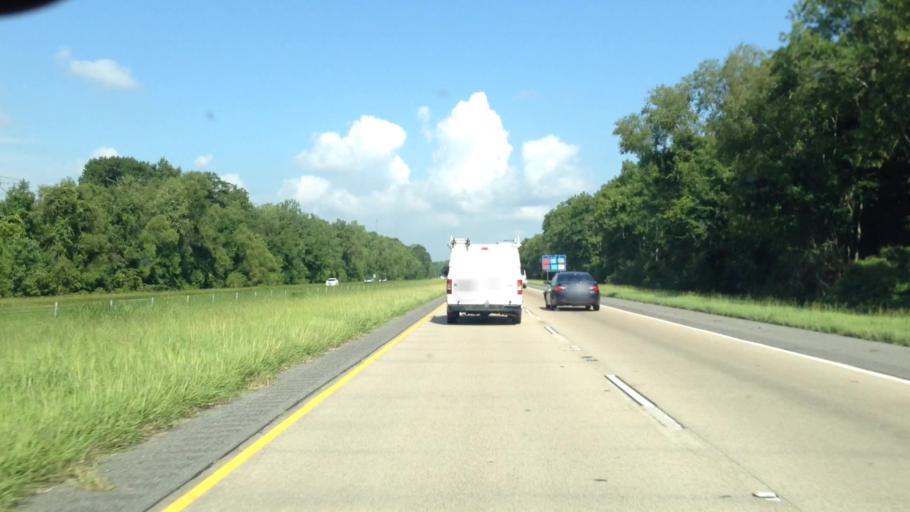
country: US
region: Louisiana
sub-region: Ascension Parish
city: Sorrento
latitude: 30.1679
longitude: -90.8636
